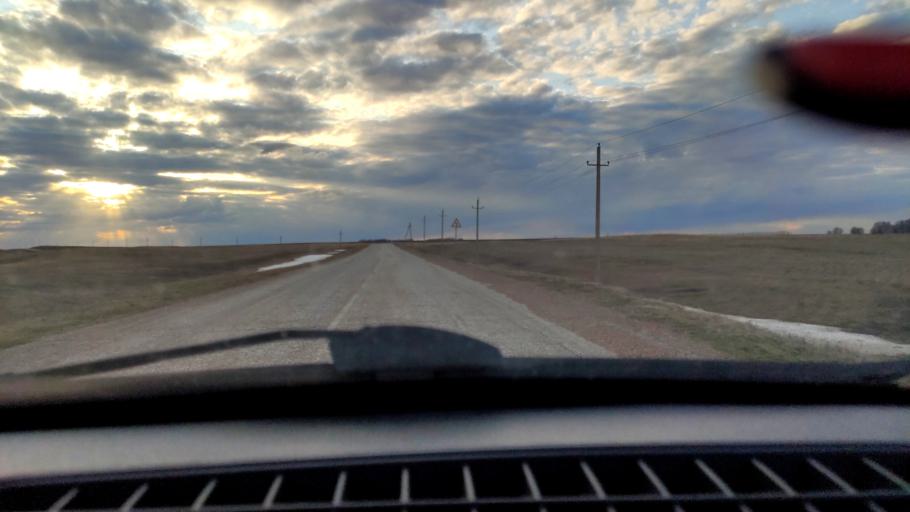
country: RU
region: Bashkortostan
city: Tolbazy
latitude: 54.0033
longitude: 55.6512
